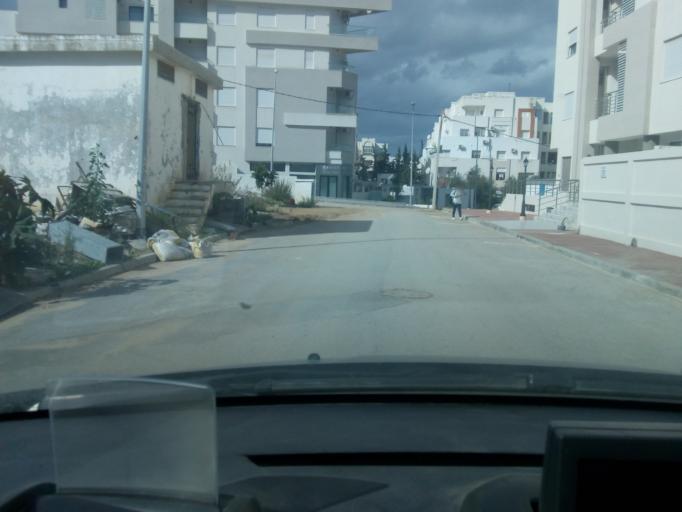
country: TN
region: Ariana
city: Ariana
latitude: 36.8771
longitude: 10.1782
